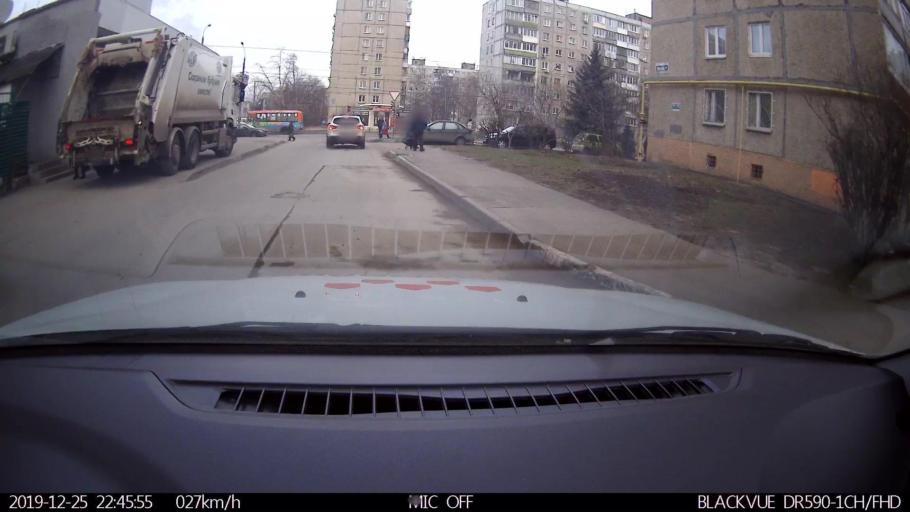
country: RU
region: Nizjnij Novgorod
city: Neklyudovo
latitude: 56.3485
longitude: 43.8579
